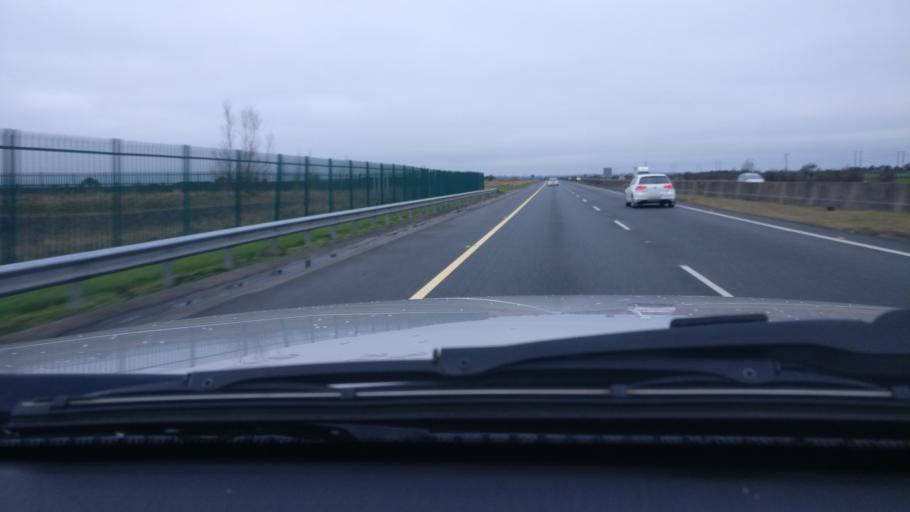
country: IE
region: Connaught
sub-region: County Galway
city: Oranmore
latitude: 53.2998
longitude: -8.8738
